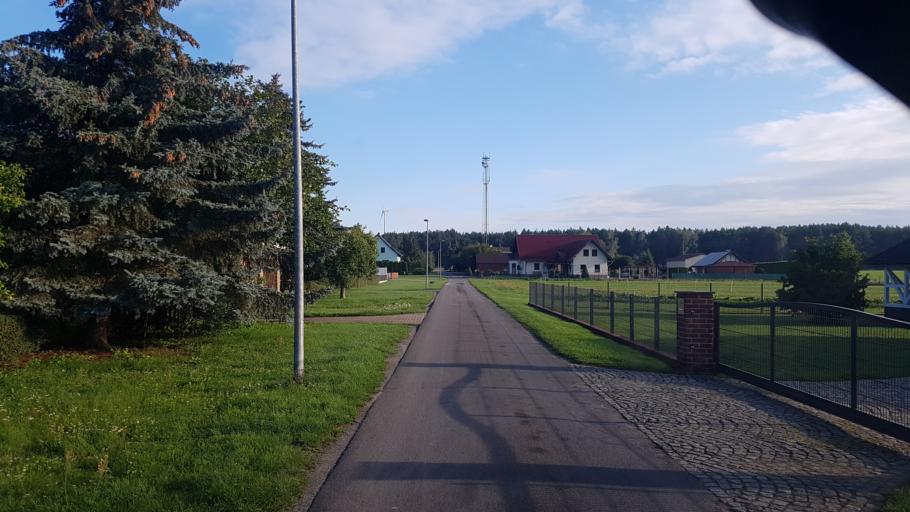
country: DE
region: Brandenburg
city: Bronkow
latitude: 51.6732
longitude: 13.8916
